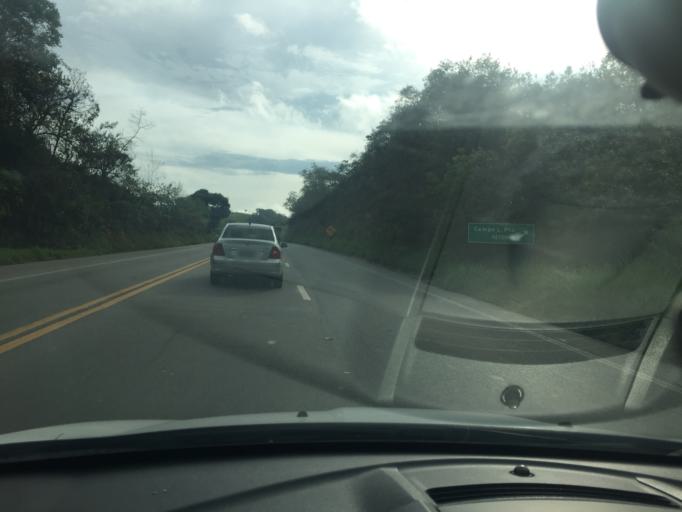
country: BR
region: Sao Paulo
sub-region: Campo Limpo Paulista
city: Campo Limpo Paulista
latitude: -23.1928
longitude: -46.7881
